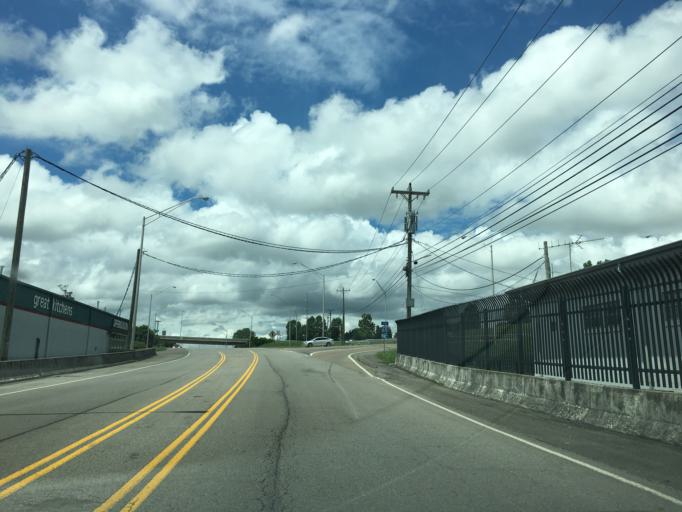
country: US
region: Tennessee
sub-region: Davidson County
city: Oak Hill
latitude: 36.1004
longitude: -86.7611
